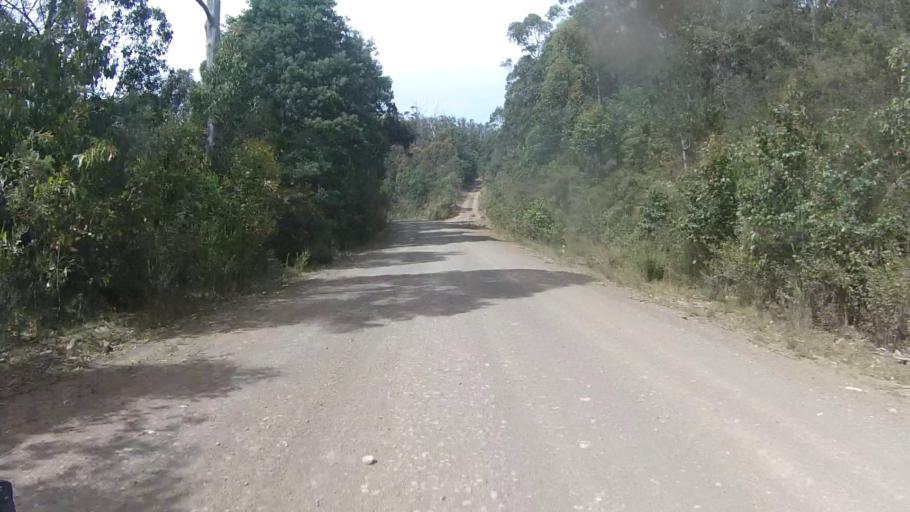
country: AU
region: Tasmania
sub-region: Sorell
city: Sorell
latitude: -42.7594
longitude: 147.8292
